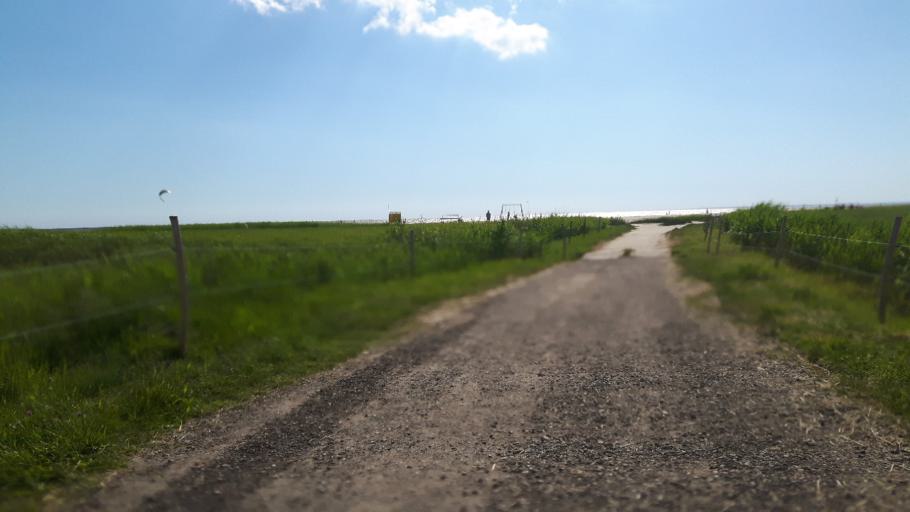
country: EE
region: Paernumaa
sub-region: Paernu linn
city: Parnu
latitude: 58.3459
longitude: 24.5616
